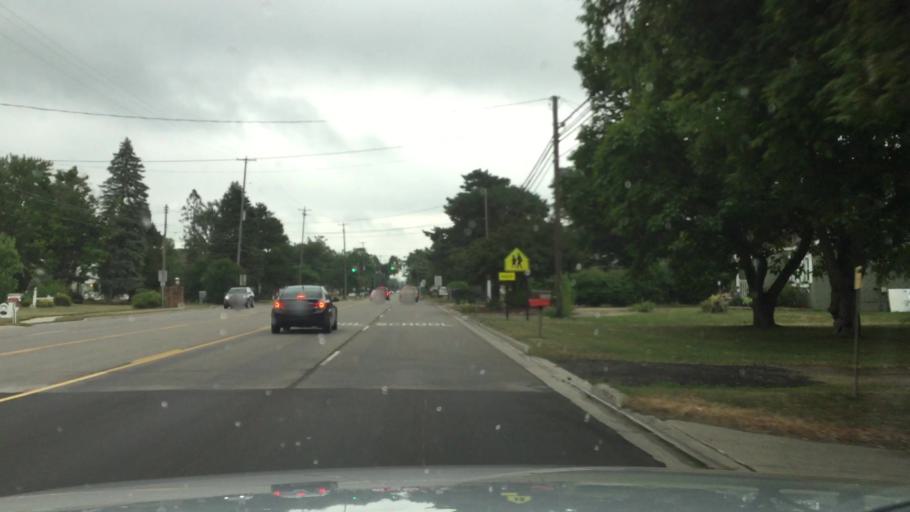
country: US
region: Michigan
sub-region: Genesee County
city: Davison
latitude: 43.0344
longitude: -83.5301
